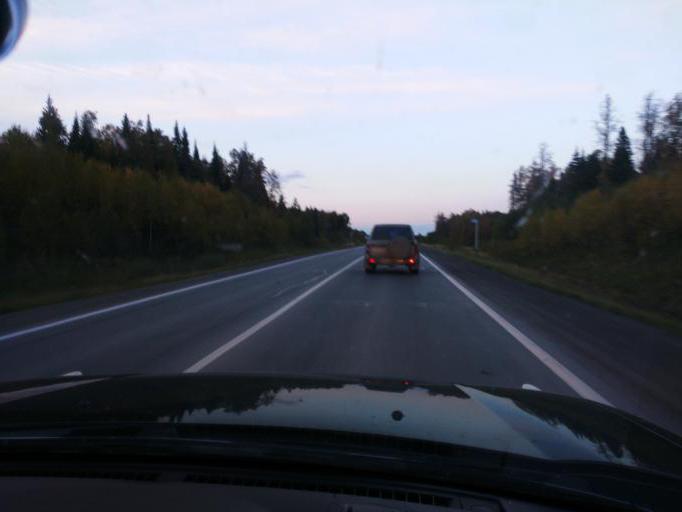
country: RU
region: Perm
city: Sylva
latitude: 58.2885
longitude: 56.7443
